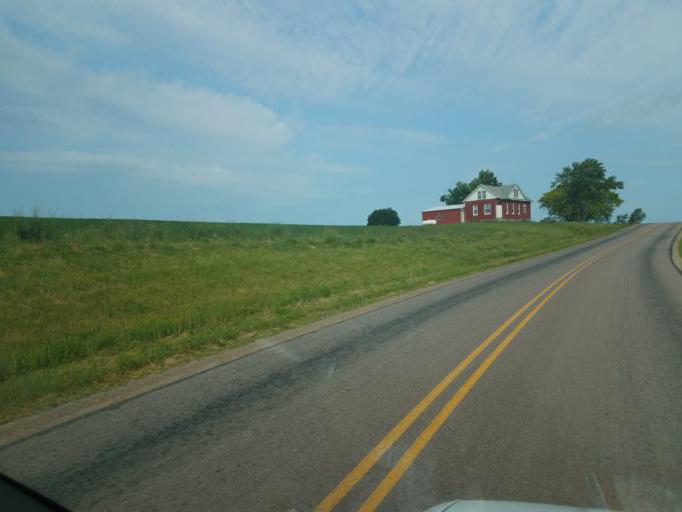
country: US
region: Wisconsin
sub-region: Vernon County
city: Hillsboro
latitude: 43.6063
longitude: -90.4334
